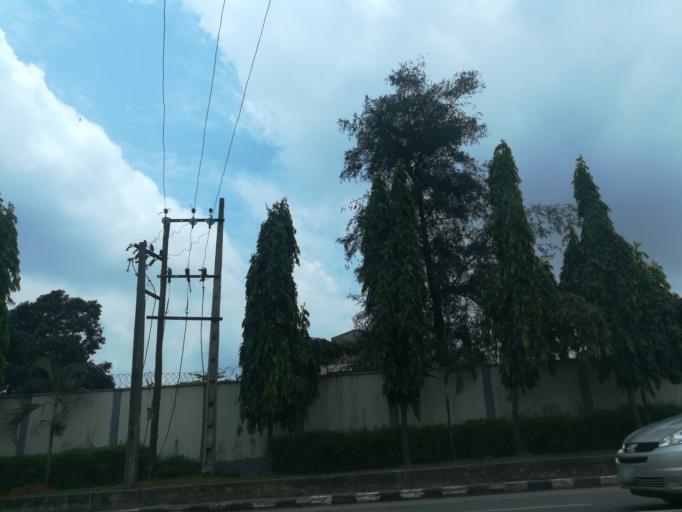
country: NG
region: Lagos
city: Ojota
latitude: 6.5917
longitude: 3.3733
